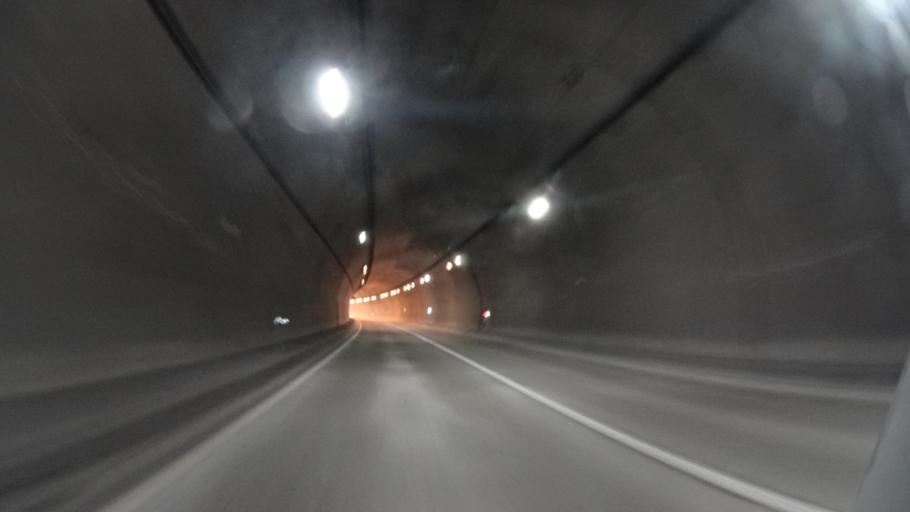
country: JP
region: Fukui
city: Tsuruga
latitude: 35.6198
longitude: 136.0830
